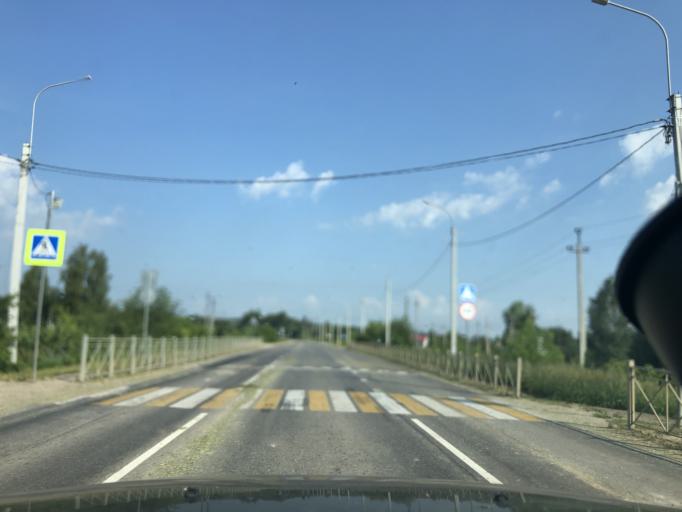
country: RU
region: Tula
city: Dubna
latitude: 54.1061
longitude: 37.1081
